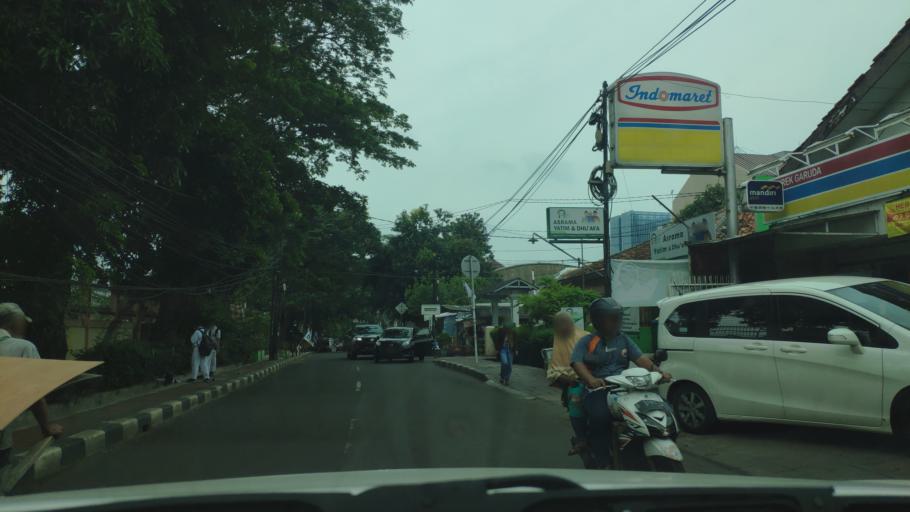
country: ID
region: Jakarta Raya
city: Jakarta
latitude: -6.1921
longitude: 106.7955
